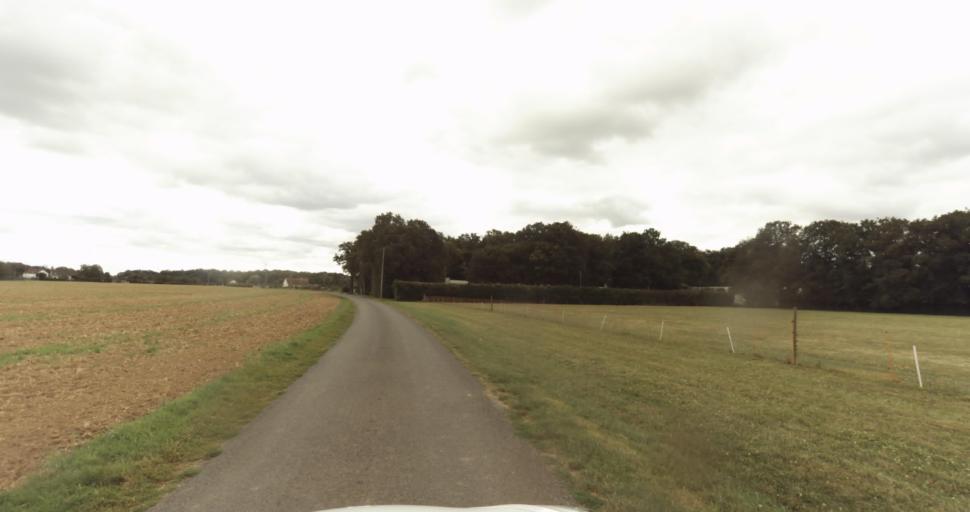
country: FR
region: Haute-Normandie
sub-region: Departement de l'Eure
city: La Madeleine-de-Nonancourt
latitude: 48.8133
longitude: 1.2101
